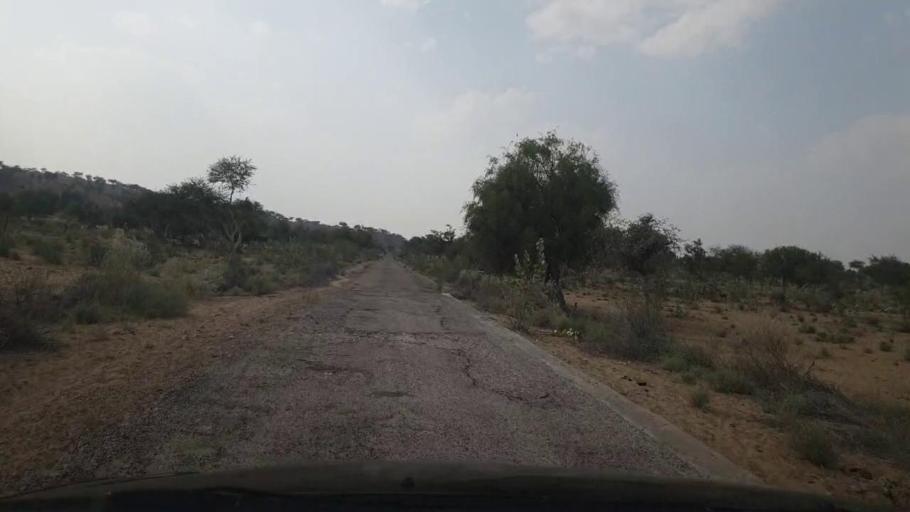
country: PK
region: Sindh
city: Islamkot
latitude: 24.9642
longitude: 70.6091
